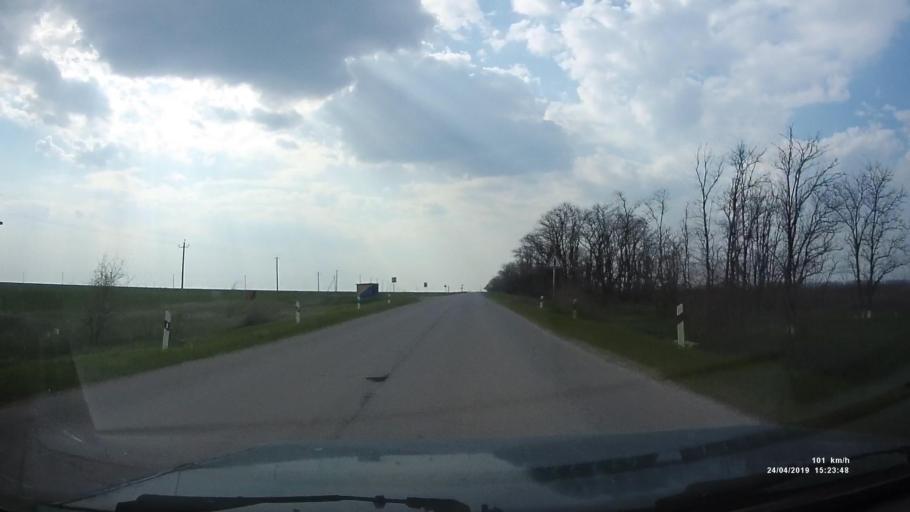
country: RU
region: Rostov
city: Remontnoye
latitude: 46.5446
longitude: 43.0821
